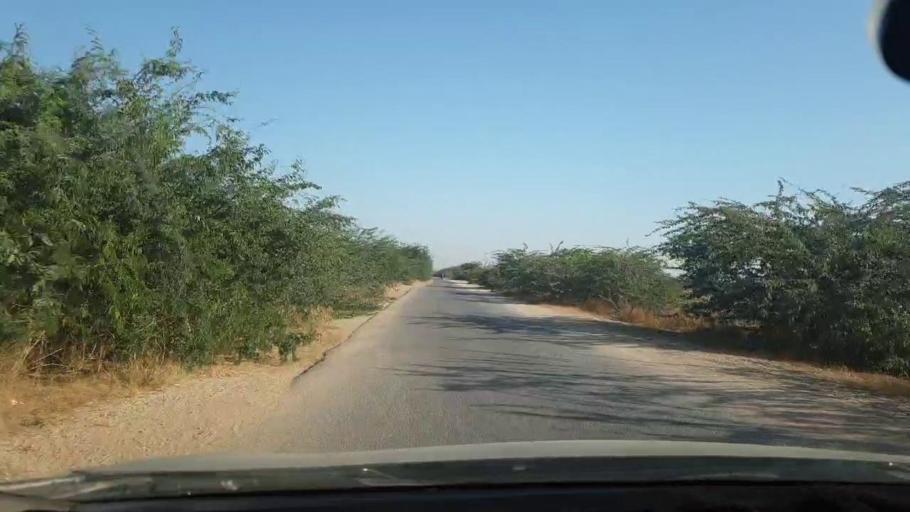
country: PK
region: Sindh
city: Malir Cantonment
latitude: 25.1633
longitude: 67.1954
